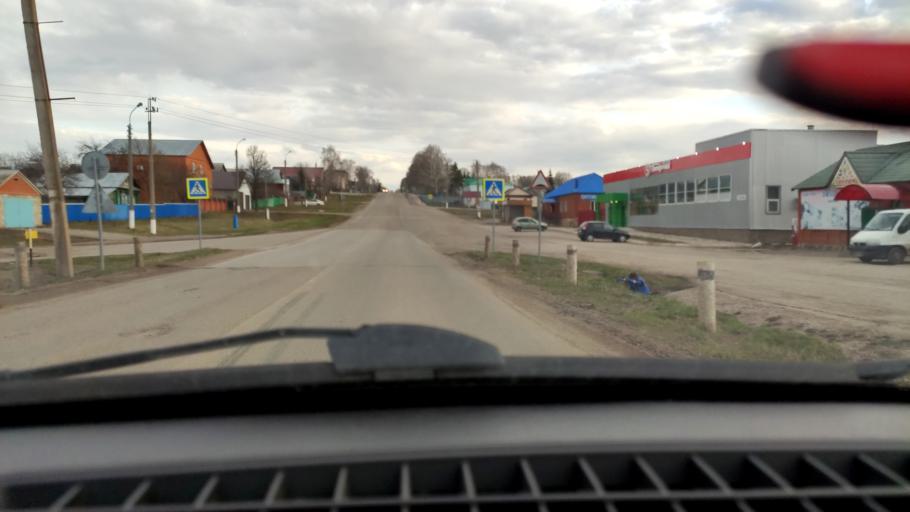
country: RU
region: Bashkortostan
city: Tolbazy
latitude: 54.0228
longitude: 55.8863
